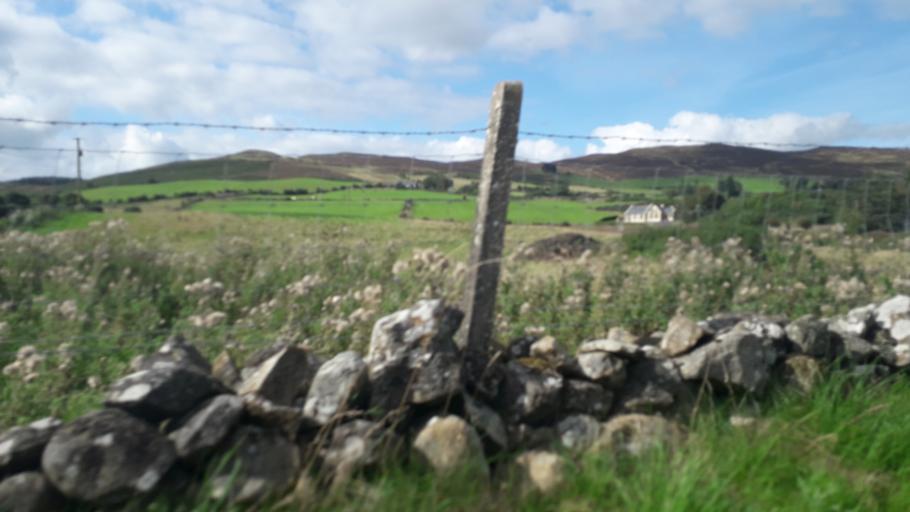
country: GB
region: Northern Ireland
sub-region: Down District
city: Warrenpoint
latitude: 54.0297
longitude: -6.2817
